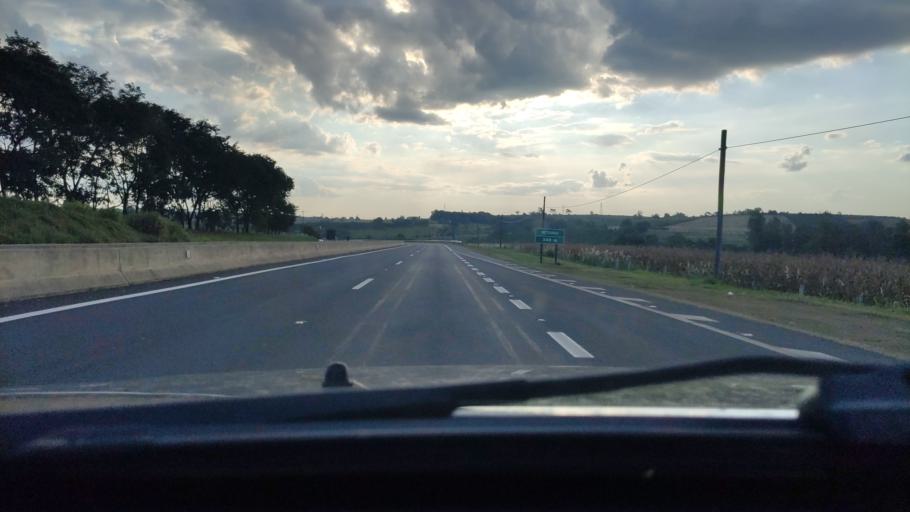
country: BR
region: Sao Paulo
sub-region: Mogi-Mirim
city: Mogi Mirim
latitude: -22.4419
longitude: -47.0459
